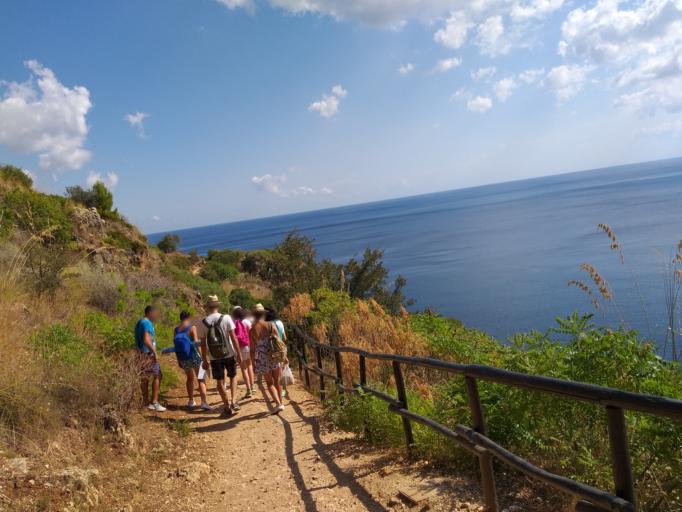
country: IT
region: Sicily
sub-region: Trapani
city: Castelluzzo
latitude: 38.0835
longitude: 12.8073
